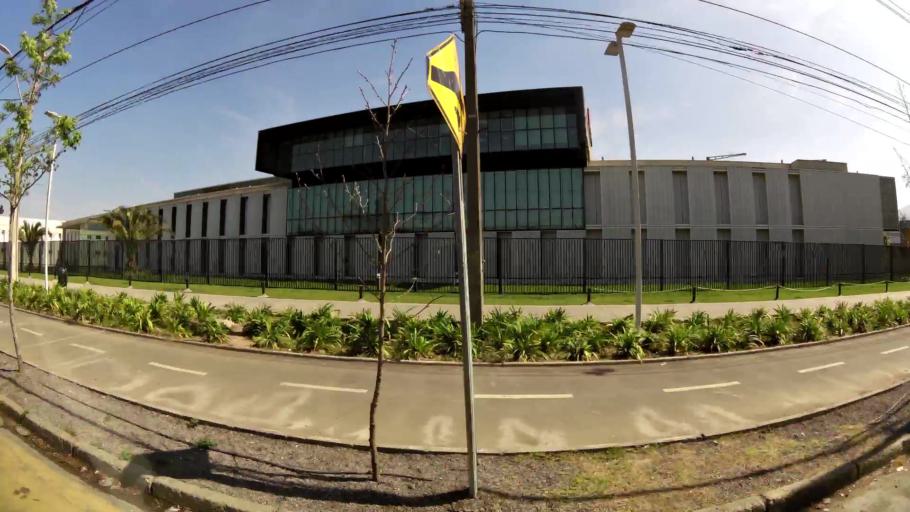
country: CL
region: Santiago Metropolitan
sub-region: Provincia de Santiago
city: Lo Prado
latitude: -33.4050
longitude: -70.6824
